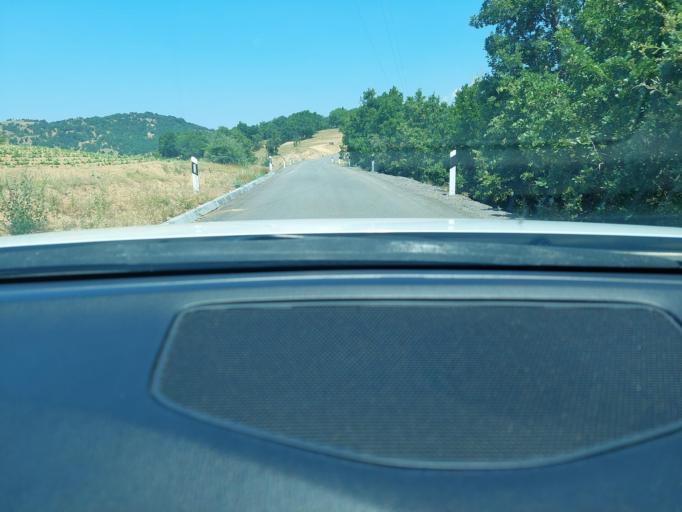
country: MK
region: Radovis
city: Radovish
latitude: 41.6635
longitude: 22.4091
